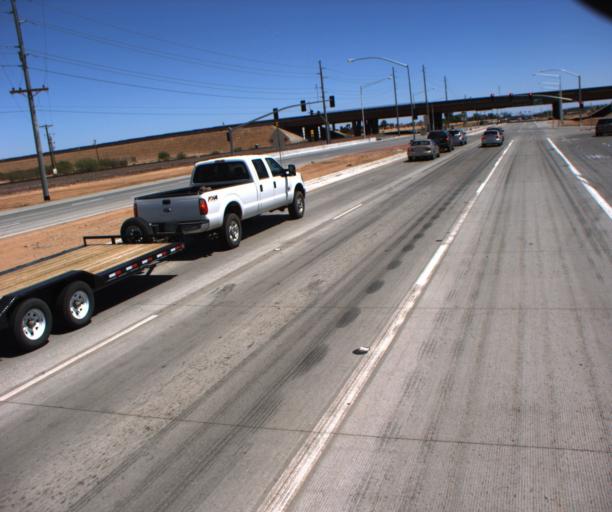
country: US
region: Arizona
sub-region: Maricopa County
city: Sun City West
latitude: 33.6823
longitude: -112.4064
